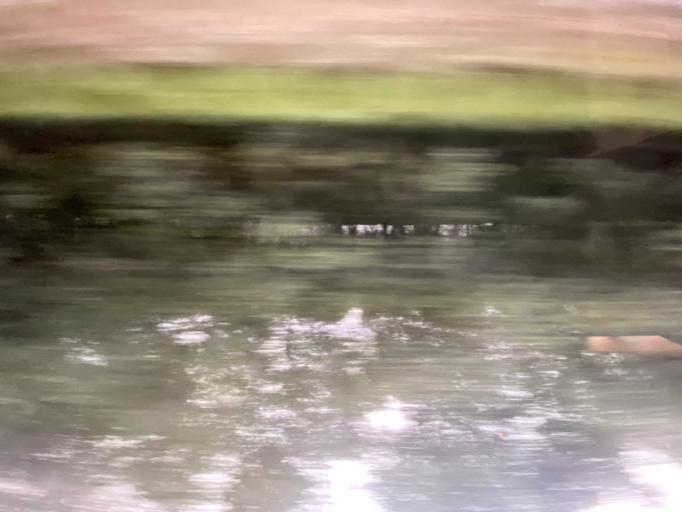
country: US
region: West Virginia
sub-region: Mineral County
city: Fort Ashby
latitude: 39.5231
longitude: -78.5751
